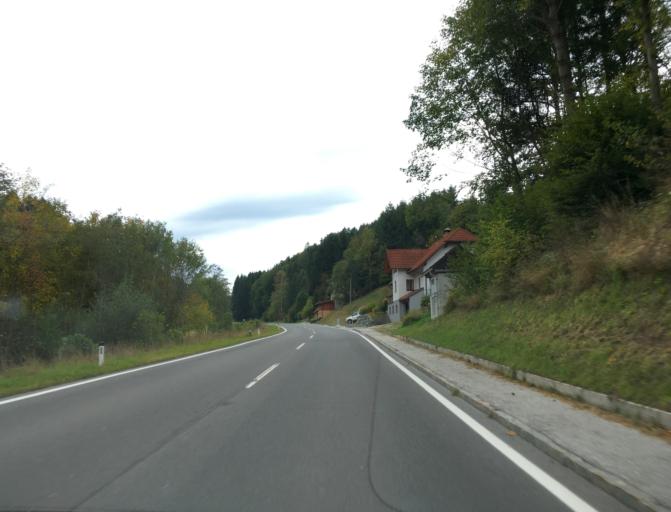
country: AT
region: Lower Austria
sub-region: Politischer Bezirk Neunkirchen
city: Thomasberg
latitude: 47.5642
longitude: 16.1424
